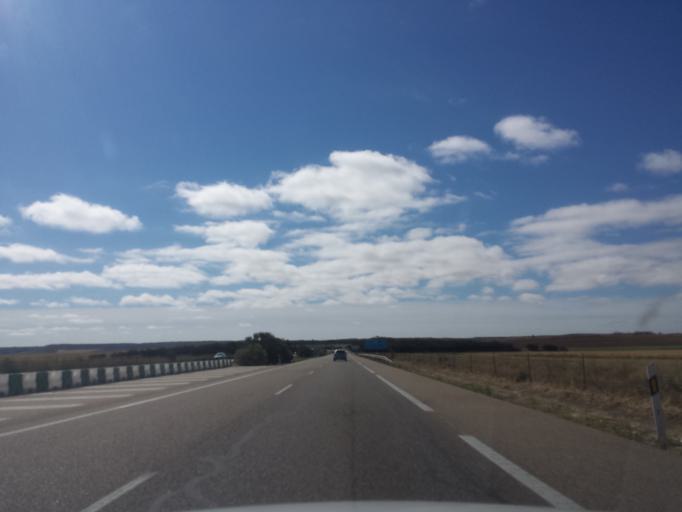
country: ES
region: Castille and Leon
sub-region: Provincia de Valladolid
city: Villardefrades
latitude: 41.7382
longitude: -5.2682
